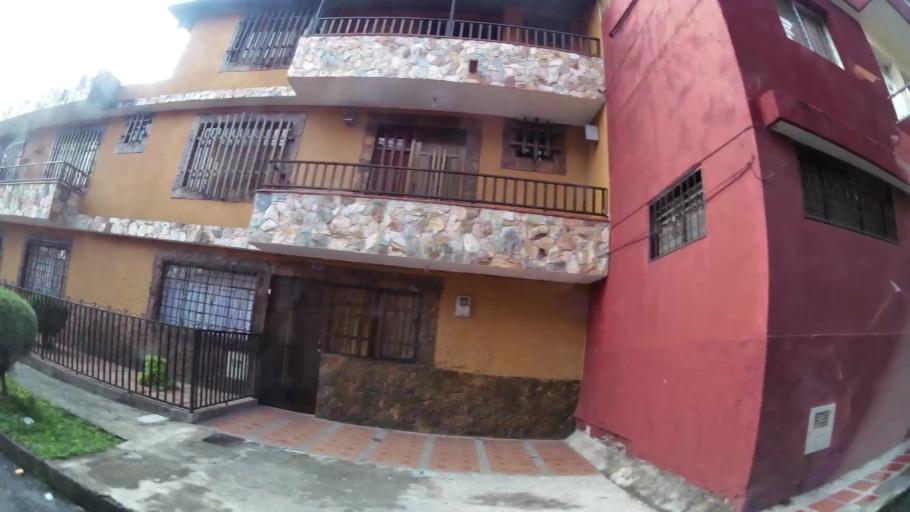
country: CO
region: Antioquia
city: Sabaneta
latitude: 6.1680
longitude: -75.6251
